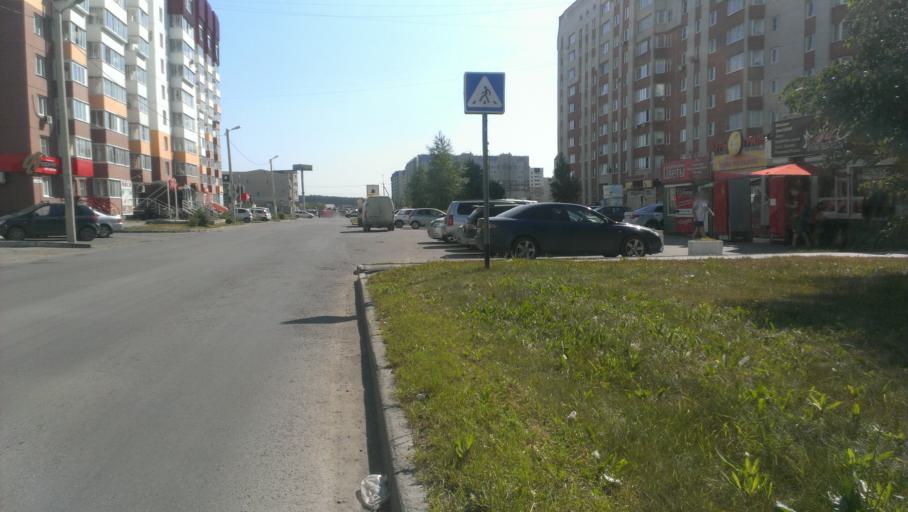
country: RU
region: Altai Krai
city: Novosilikatnyy
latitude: 53.3315
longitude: 83.6846
